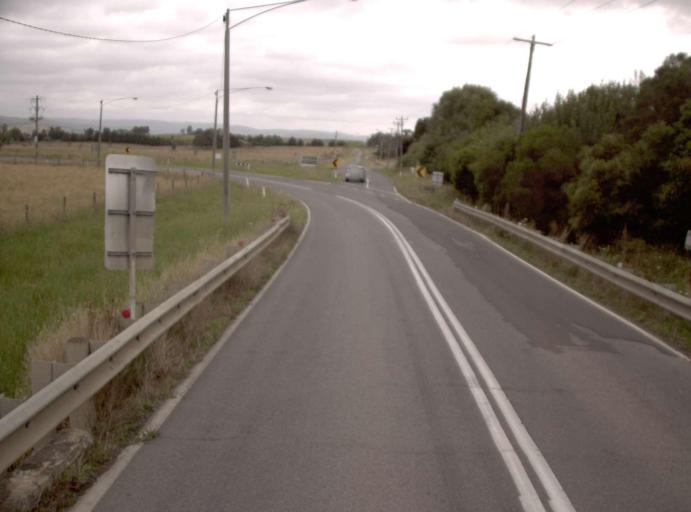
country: AU
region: Victoria
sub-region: Yarra Ranges
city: Yarra Glen
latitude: -37.6936
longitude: 145.3842
